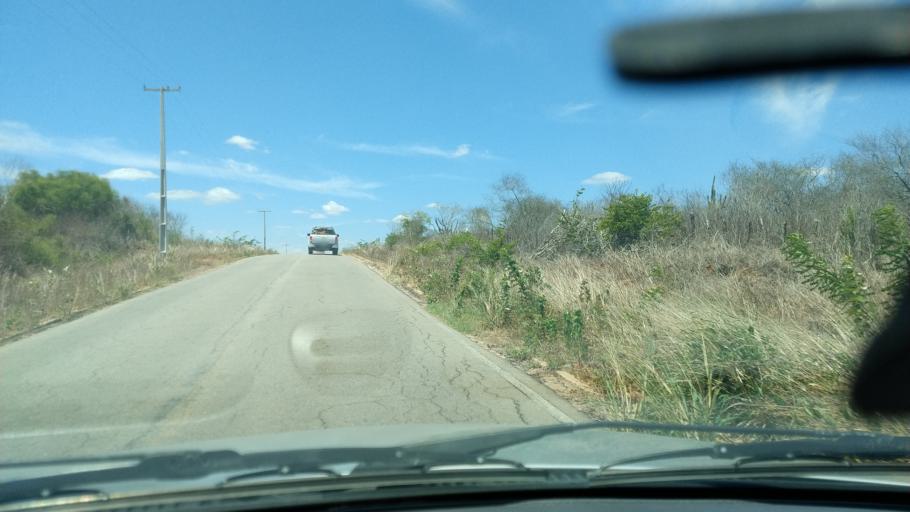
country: BR
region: Rio Grande do Norte
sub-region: Sao Paulo Do Potengi
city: Sao Paulo do Potengi
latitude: -5.9138
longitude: -35.5911
